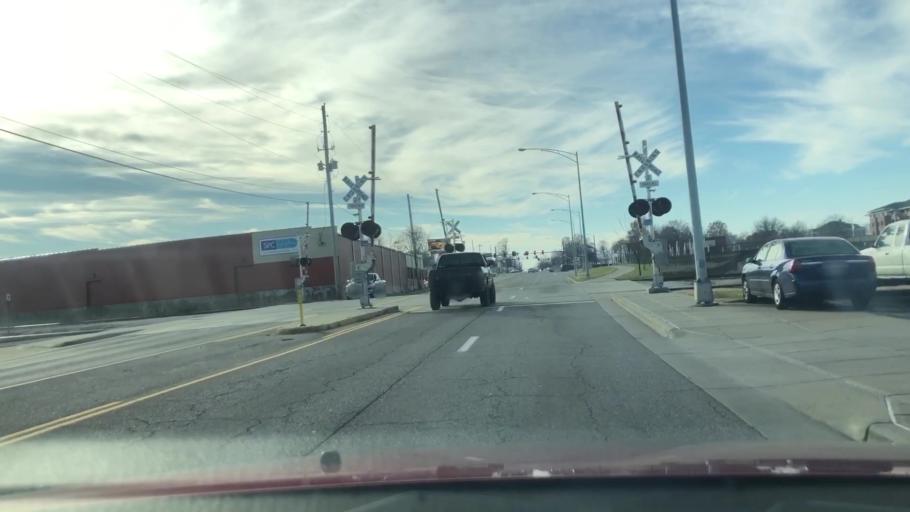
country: US
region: Missouri
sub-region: Greene County
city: Springfield
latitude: 37.2128
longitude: -93.2759
